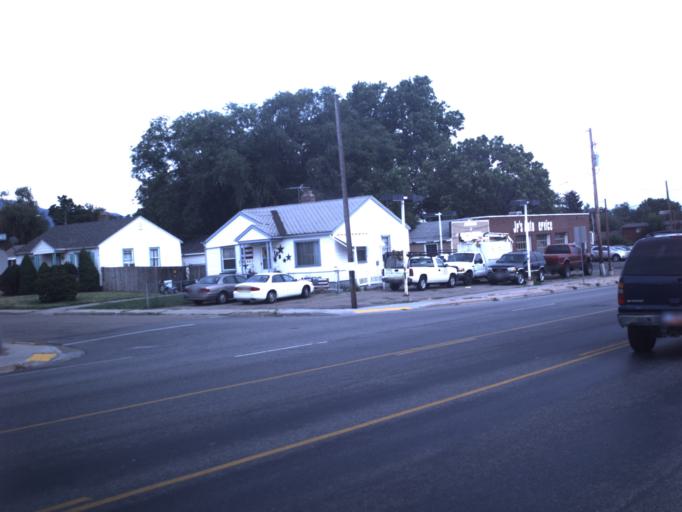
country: US
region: Utah
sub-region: Davis County
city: Clearfield
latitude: 41.1174
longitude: -112.0261
